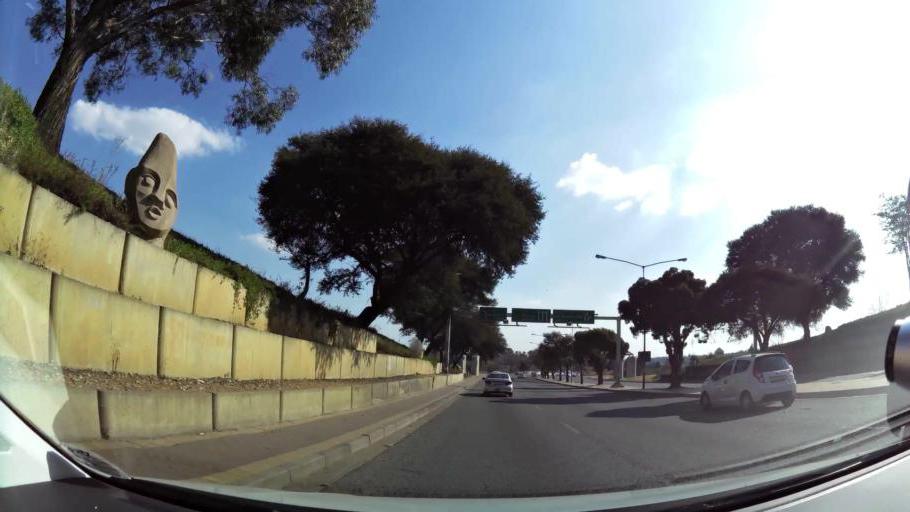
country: ZA
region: Gauteng
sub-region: City of Johannesburg Metropolitan Municipality
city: Modderfontein
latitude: -26.1011
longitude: 28.2225
